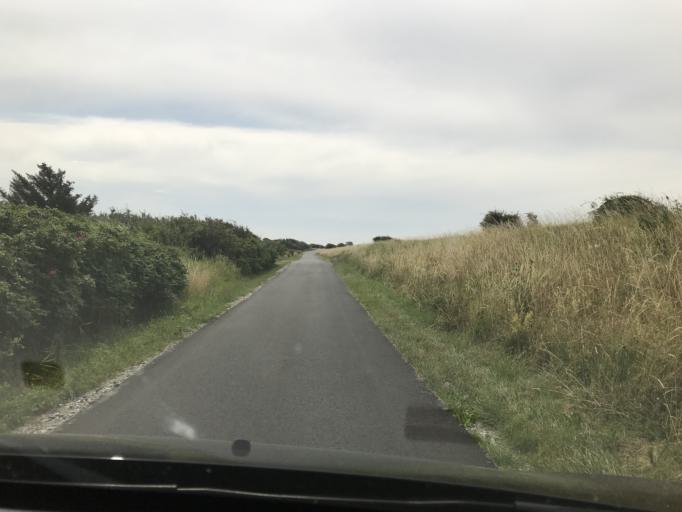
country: DK
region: South Denmark
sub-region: AEro Kommune
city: AEroskobing
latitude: 54.9246
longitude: 10.2447
